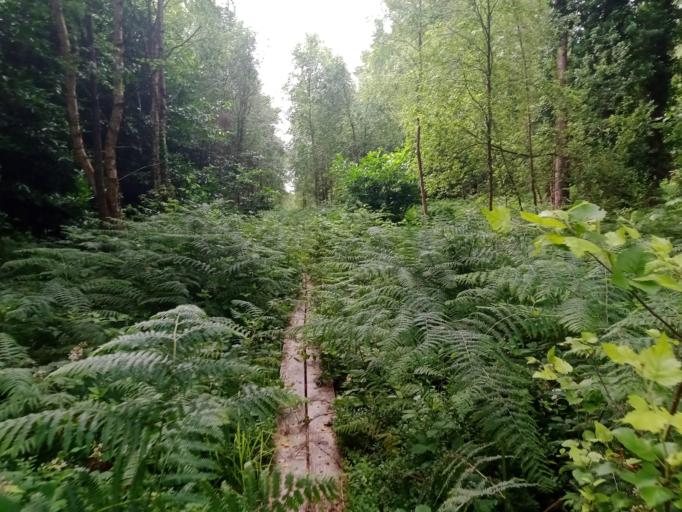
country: IE
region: Leinster
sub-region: Laois
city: Abbeyleix
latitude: 52.8894
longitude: -7.3600
